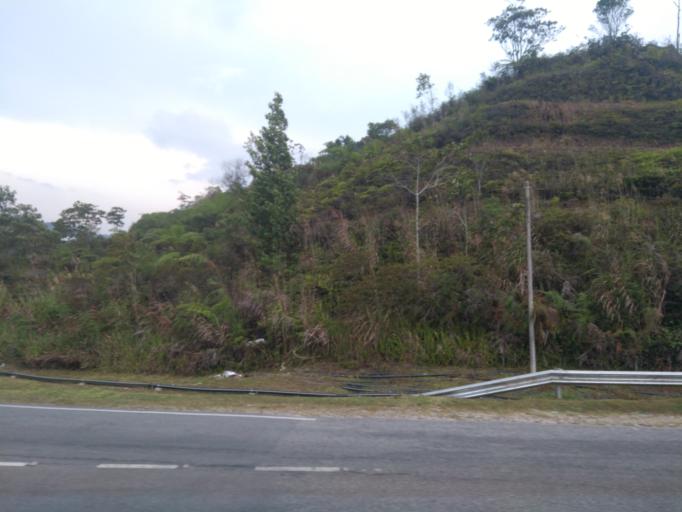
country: MY
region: Pahang
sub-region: Cameron Highlands
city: Tanah Rata
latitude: 4.5832
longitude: 101.4151
